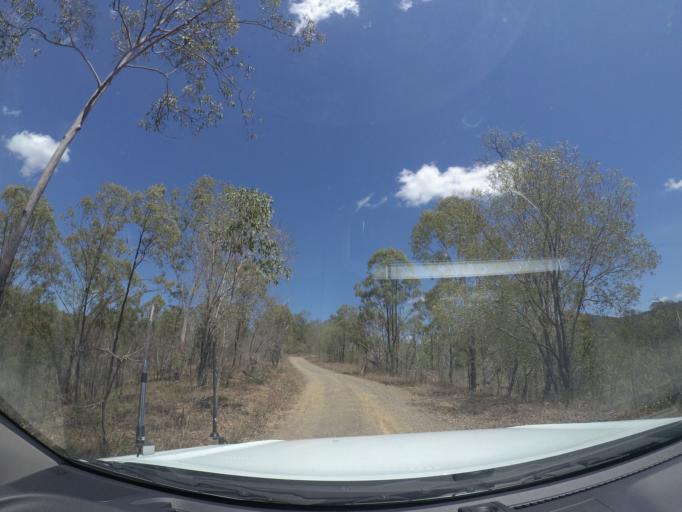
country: AU
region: Queensland
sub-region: Ipswich
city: Springfield Lakes
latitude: -27.8232
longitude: 152.8423
